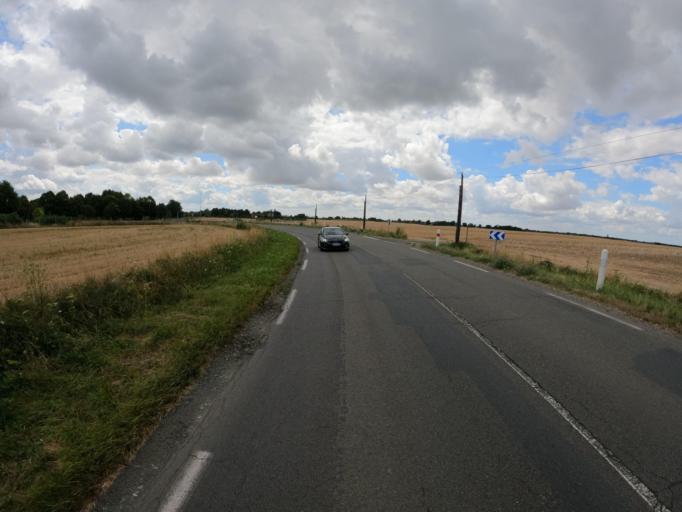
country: FR
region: Pays de la Loire
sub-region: Departement de la Sarthe
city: Sable-sur-Sarthe
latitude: 47.8567
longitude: -0.3224
